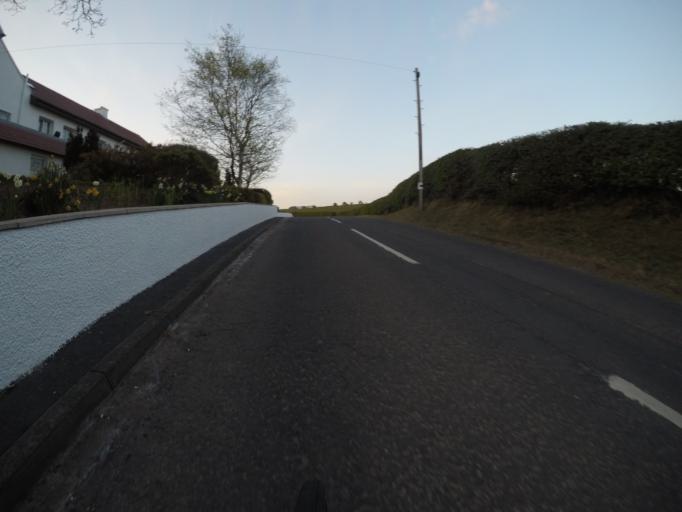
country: GB
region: Scotland
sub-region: South Ayrshire
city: Dundonald
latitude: 55.5543
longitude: -4.6177
